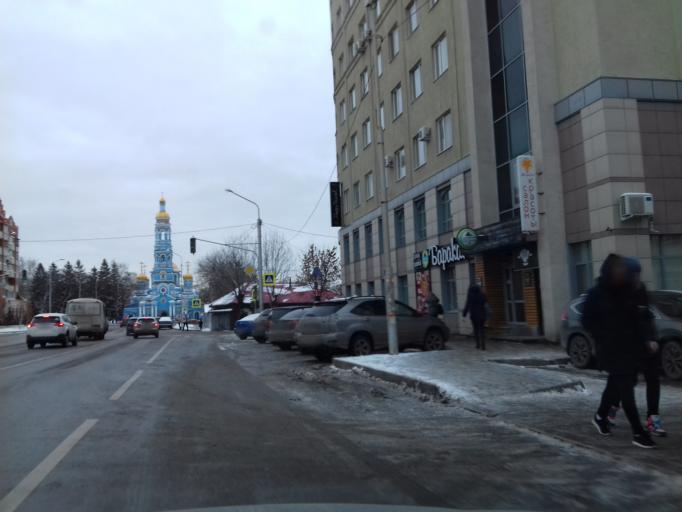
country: RU
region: Bashkortostan
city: Ufa
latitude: 54.7278
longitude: 55.9698
